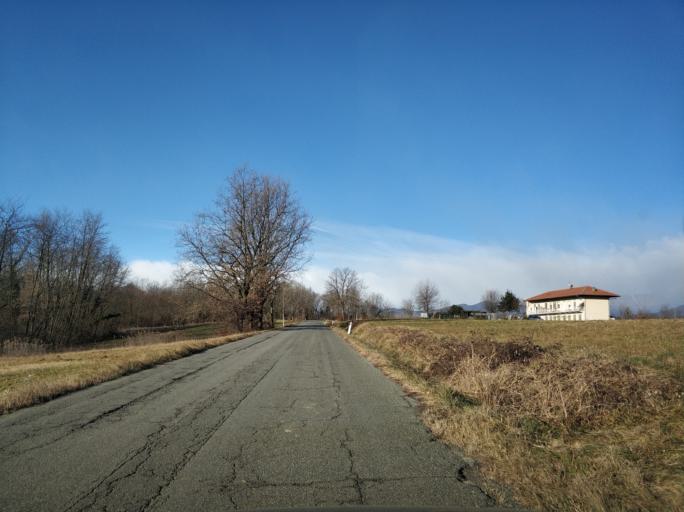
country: IT
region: Piedmont
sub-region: Provincia di Torino
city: Front
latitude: 45.2641
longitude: 7.6429
